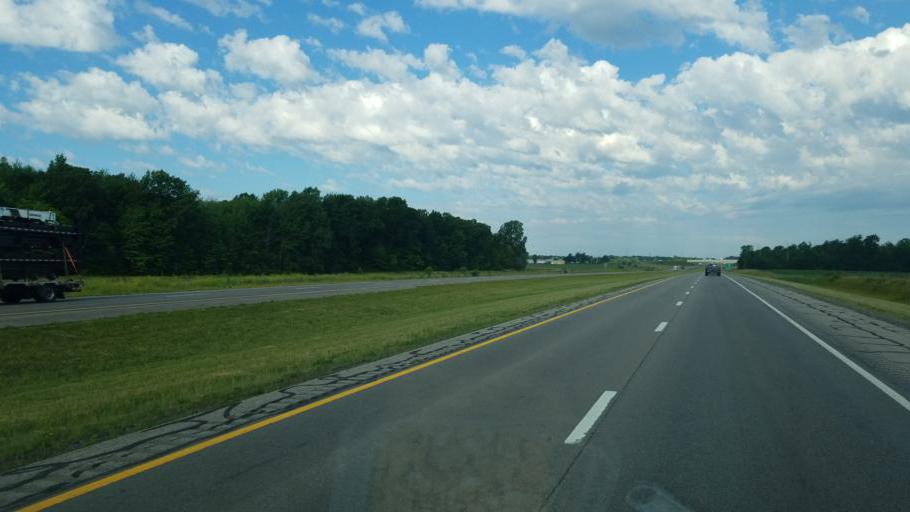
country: US
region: Ohio
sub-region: Crawford County
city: Crestline
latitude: 40.7627
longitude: -82.7321
